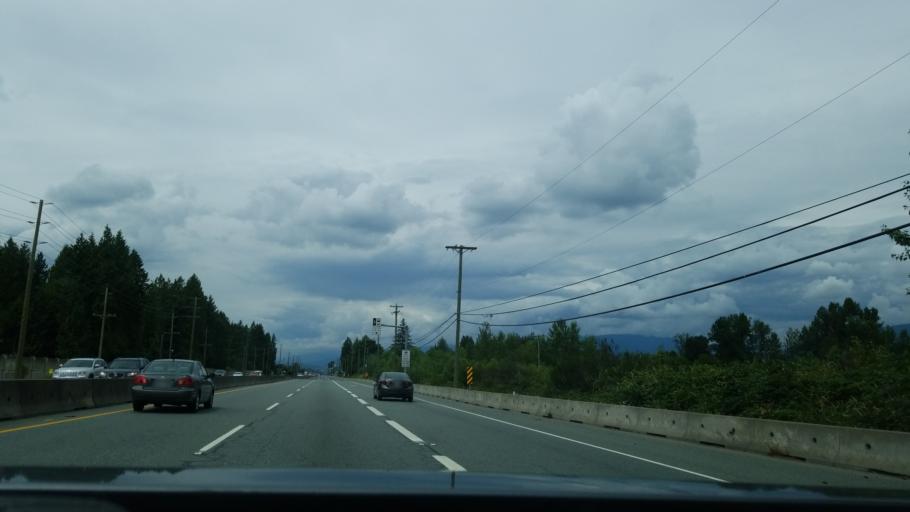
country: CA
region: British Columbia
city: Pitt Meadows
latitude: 49.2273
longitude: -122.6796
